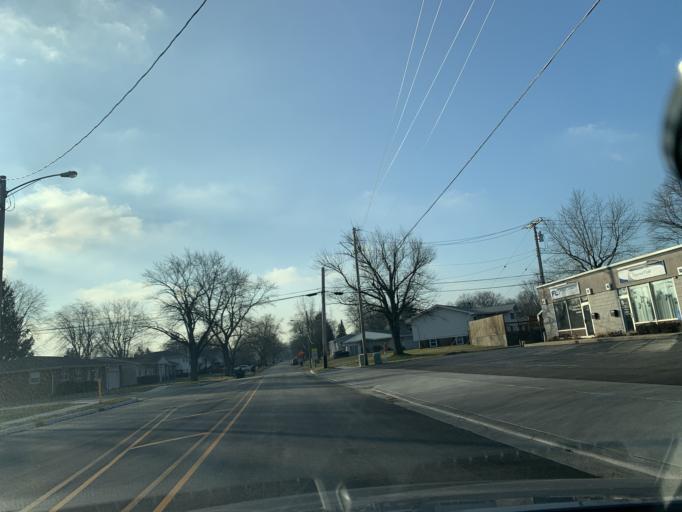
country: US
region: Indiana
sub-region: Porter County
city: Portage
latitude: 41.5754
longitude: -87.1686
